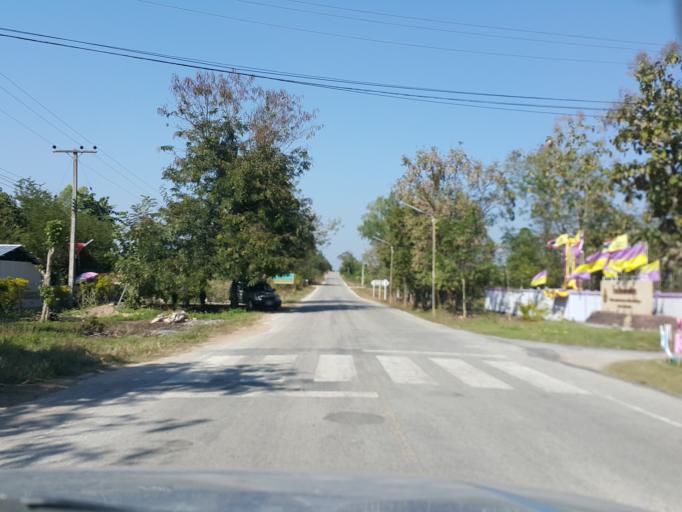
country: TH
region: Chiang Mai
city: Mae Wang
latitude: 18.5398
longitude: 98.7968
